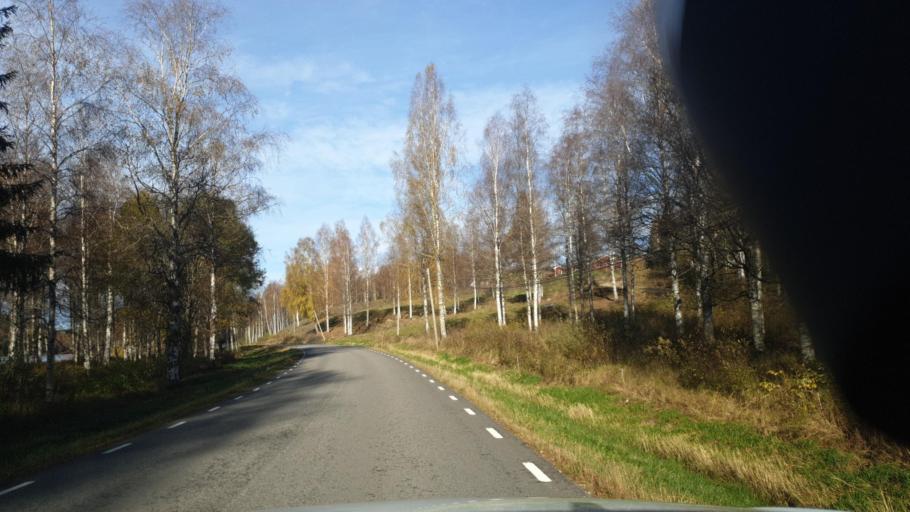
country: SE
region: Vaermland
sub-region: Eda Kommun
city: Amotfors
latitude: 59.8904
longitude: 12.5256
